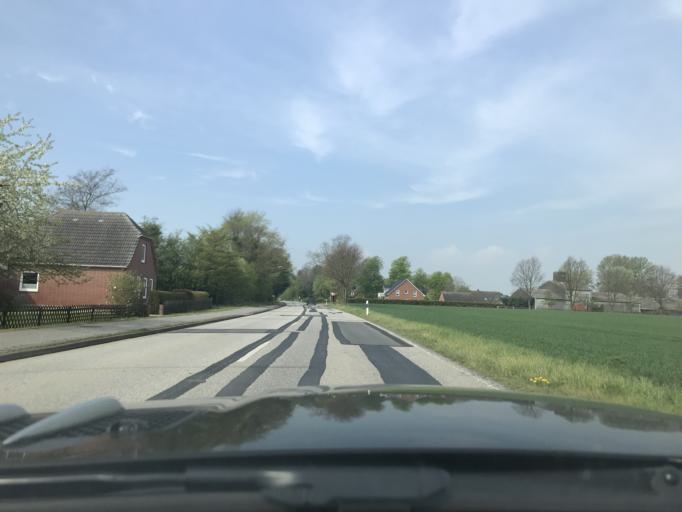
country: DE
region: Schleswig-Holstein
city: Riepsdorf
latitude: 54.1951
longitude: 10.9975
